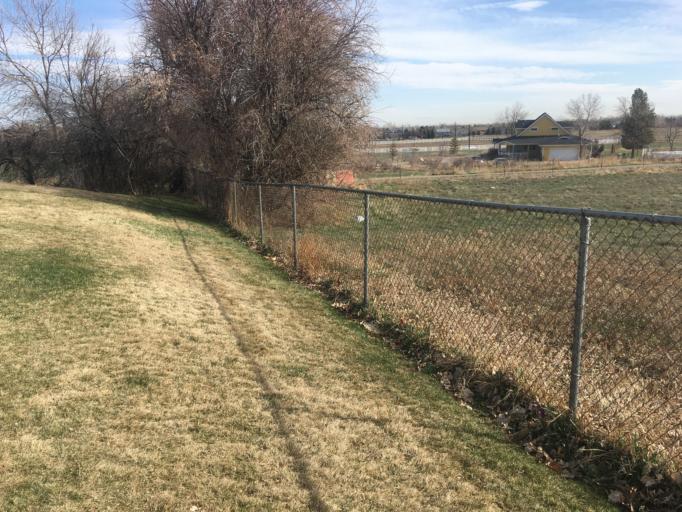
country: US
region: Colorado
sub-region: Boulder County
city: Lafayette
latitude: 40.0108
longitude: -105.0957
